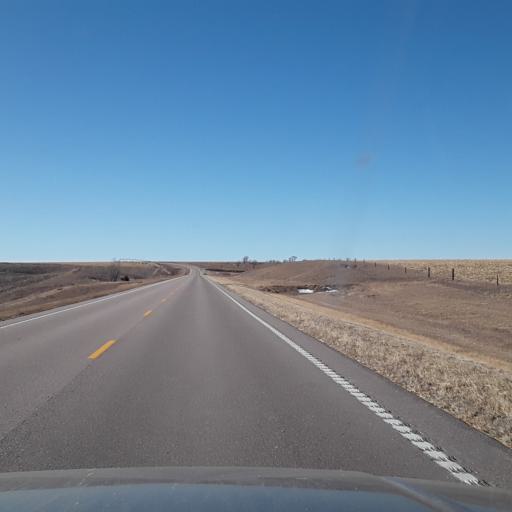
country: US
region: Nebraska
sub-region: Frontier County
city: Stockville
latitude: 40.7057
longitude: -100.2339
